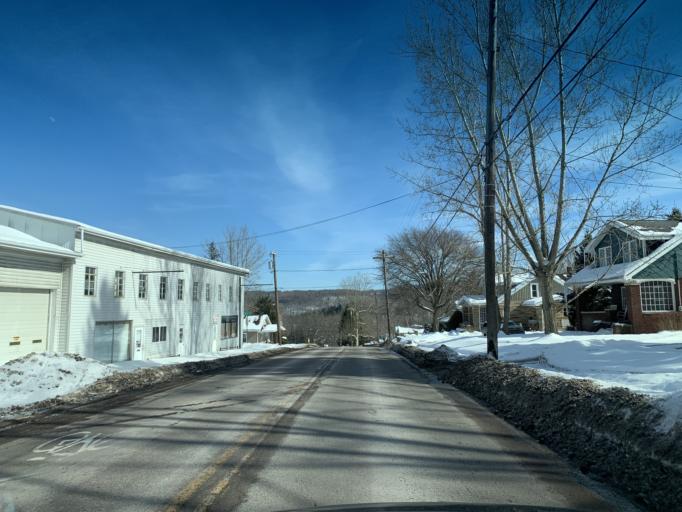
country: US
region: Pennsylvania
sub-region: Somerset County
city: Meyersdale
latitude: 39.6956
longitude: -79.1508
